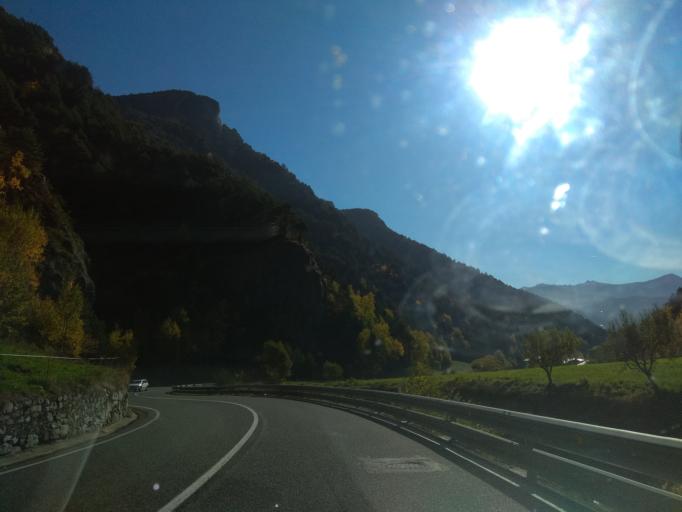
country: AD
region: La Massana
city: Arinsal
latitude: 42.5614
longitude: 1.5009
